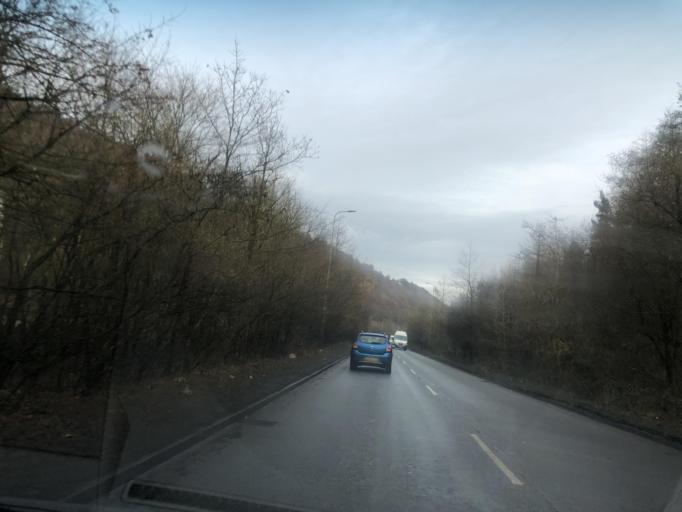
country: GB
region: Wales
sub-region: Caerphilly County Borough
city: Crumlin
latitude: 51.6831
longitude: -3.0975
